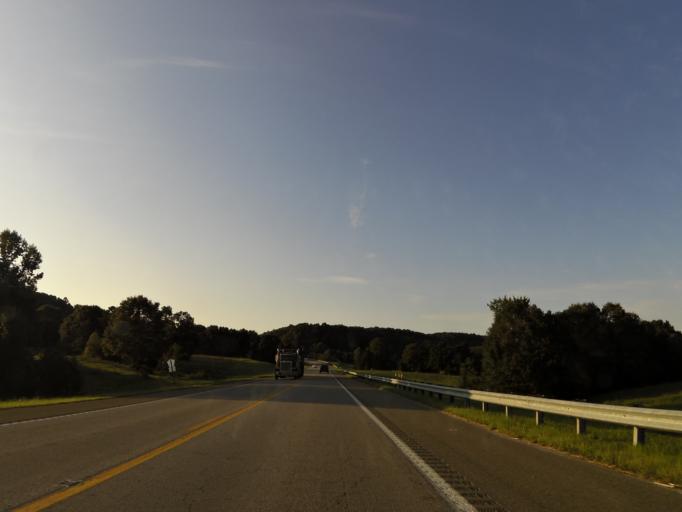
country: US
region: Tennessee
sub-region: Meigs County
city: Decatur
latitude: 35.5579
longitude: -84.6681
